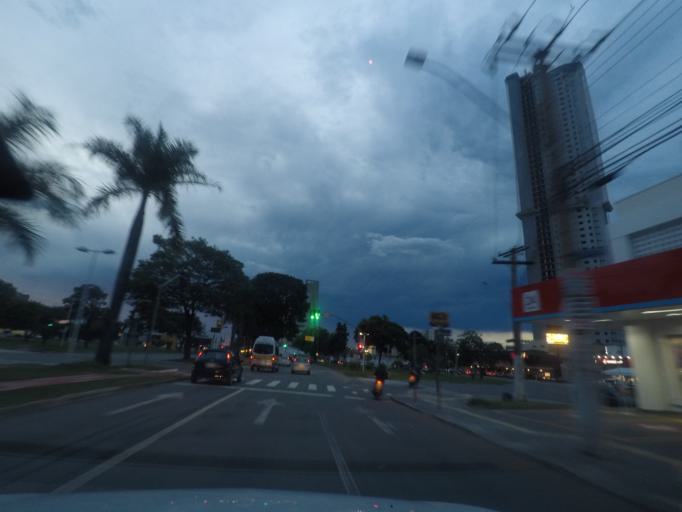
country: BR
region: Goias
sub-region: Goiania
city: Goiania
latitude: -16.7142
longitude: -49.2731
